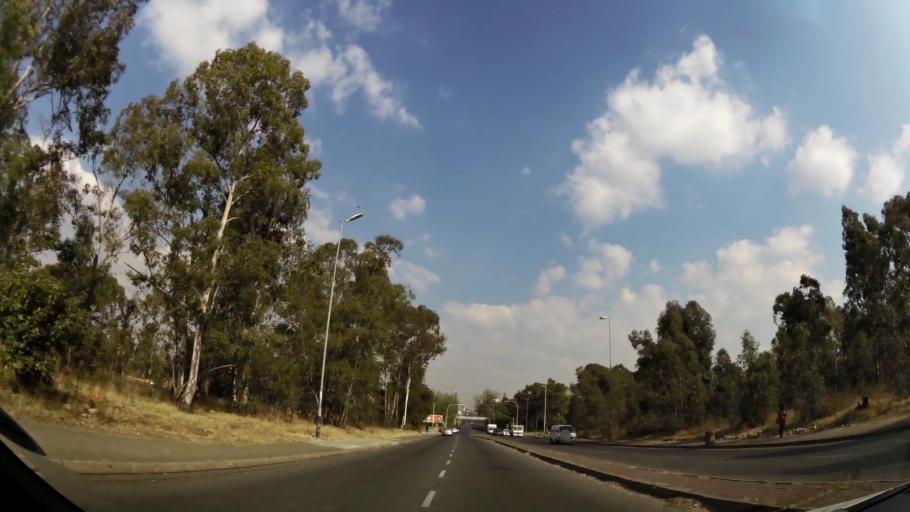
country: ZA
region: Gauteng
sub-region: Ekurhuleni Metropolitan Municipality
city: Boksburg
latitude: -26.2171
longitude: 28.2534
